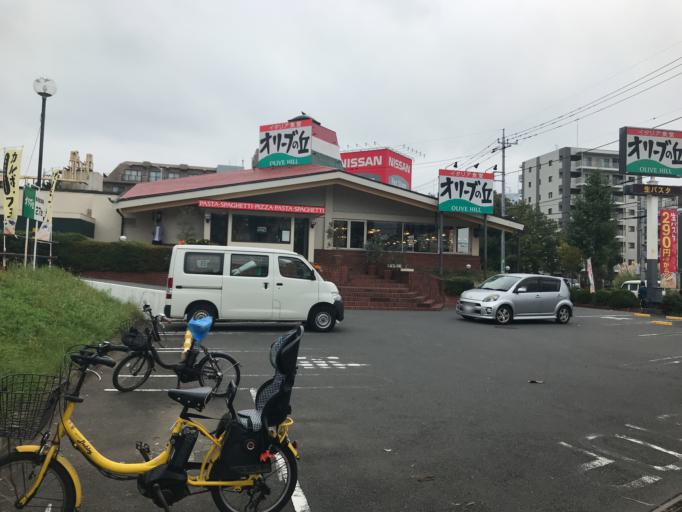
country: JP
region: Tokyo
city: Hino
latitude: 35.6350
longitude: 139.4460
